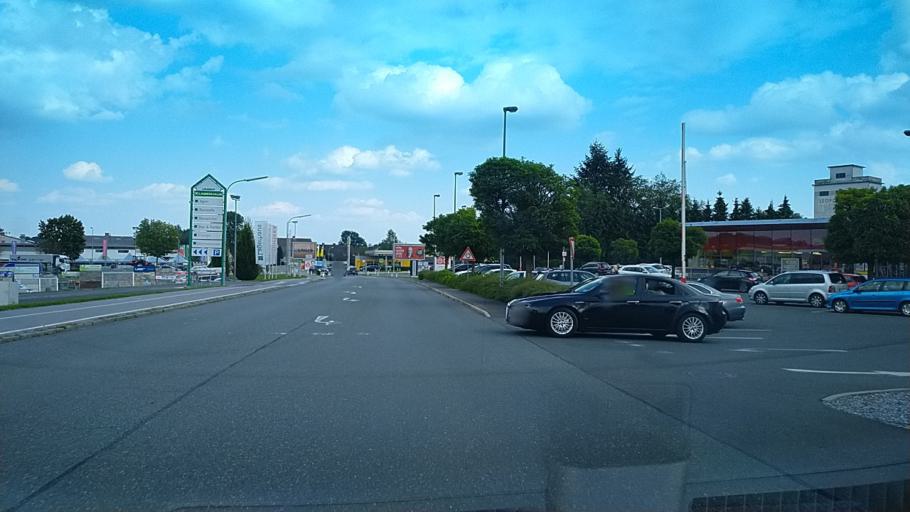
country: AT
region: Styria
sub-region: Politischer Bezirk Deutschlandsberg
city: Deutschlandsberg
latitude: 46.8207
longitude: 15.2346
